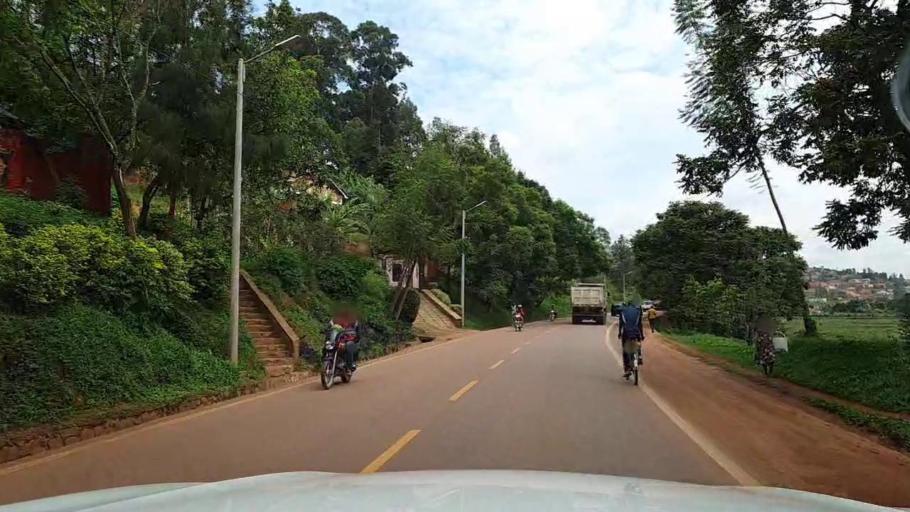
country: RW
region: Kigali
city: Kigali
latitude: -1.9091
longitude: 30.0479
